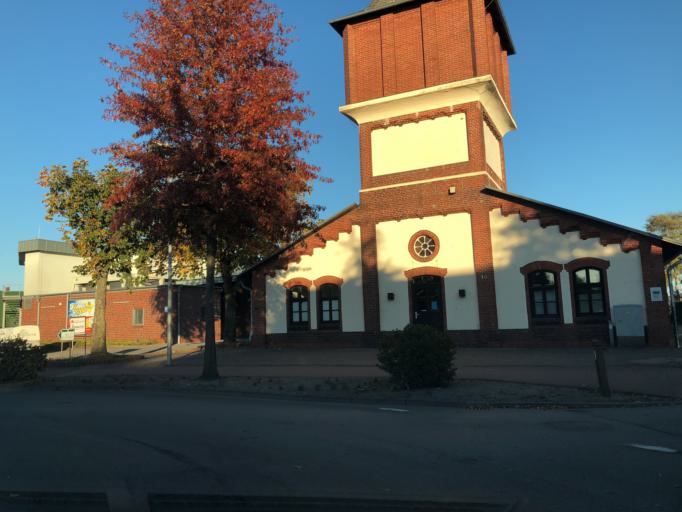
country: DE
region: Lower Saxony
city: Friesoythe
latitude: 53.0242
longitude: 7.8551
